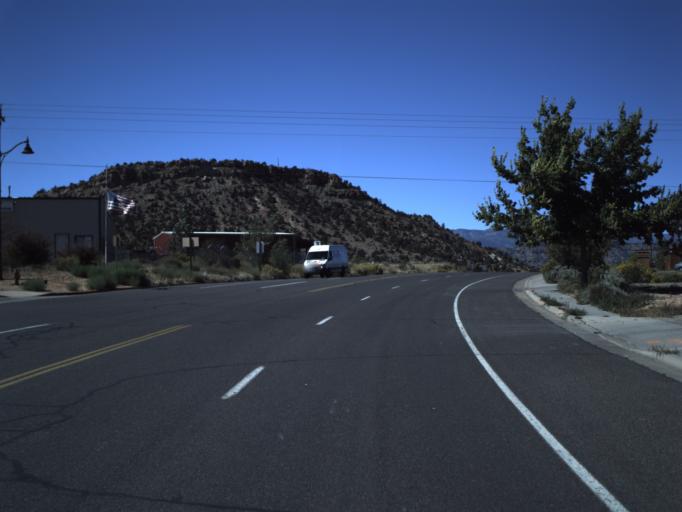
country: US
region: Utah
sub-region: Wayne County
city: Loa
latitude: 37.7706
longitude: -111.6095
